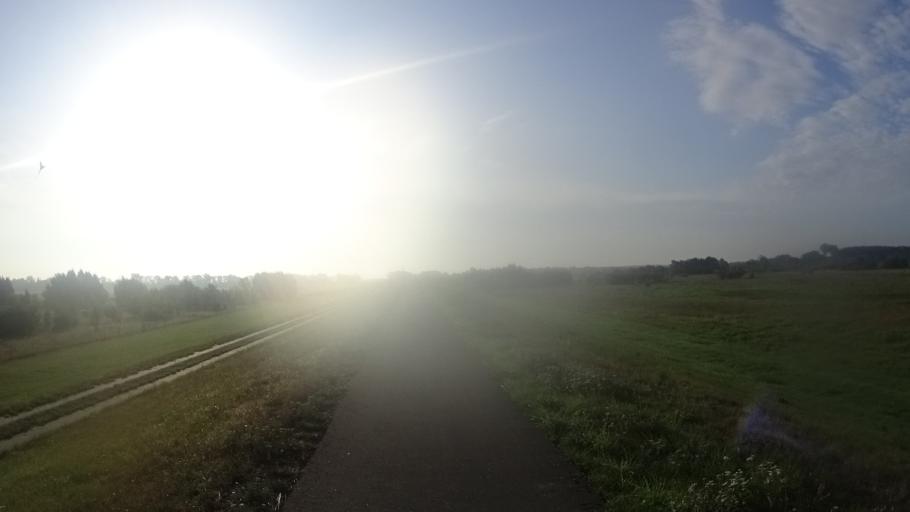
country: DE
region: Brandenburg
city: Lenzen
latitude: 53.0643
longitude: 11.5028
